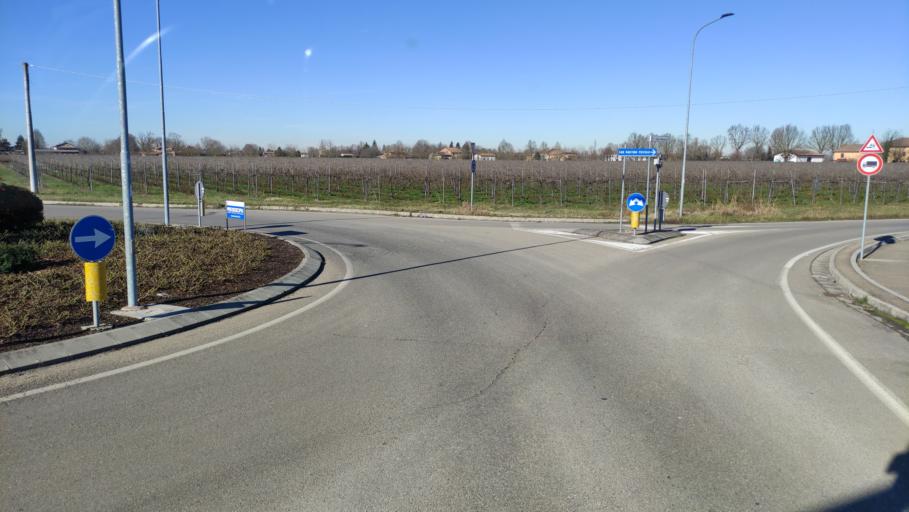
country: IT
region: Emilia-Romagna
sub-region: Provincia di Reggio Emilia
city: Correggio
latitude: 44.7771
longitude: 10.7992
